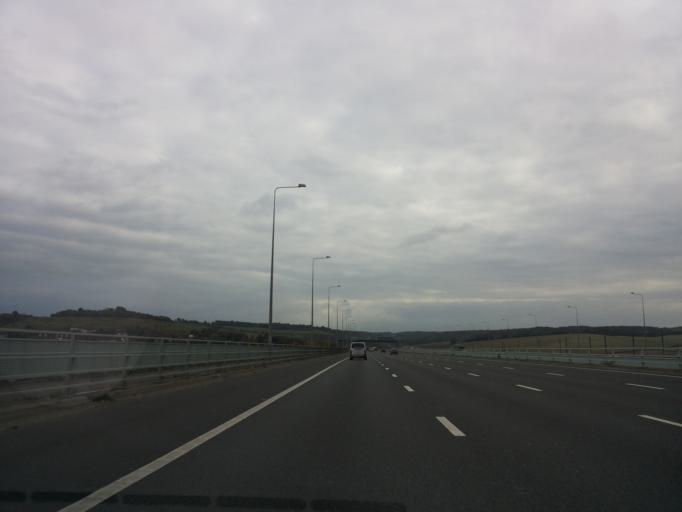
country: GB
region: England
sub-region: Medway
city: Cuxton
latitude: 51.3769
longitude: 0.4751
